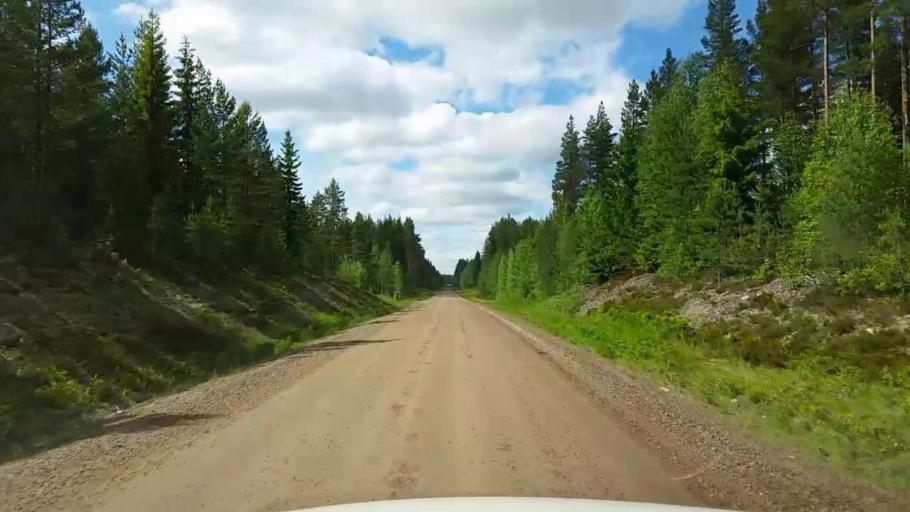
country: SE
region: Gaevleborg
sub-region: Ovanakers Kommun
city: Alfta
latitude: 61.4713
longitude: 16.0189
